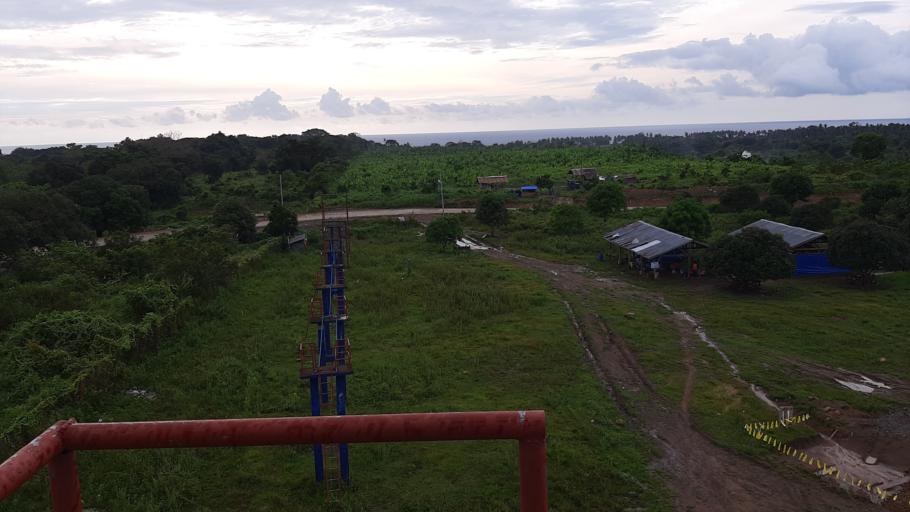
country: PH
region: Zamboanga Peninsula
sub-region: Province of  Zamboanga del Sur
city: Sinubong
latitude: 7.0099
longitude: 121.9339
